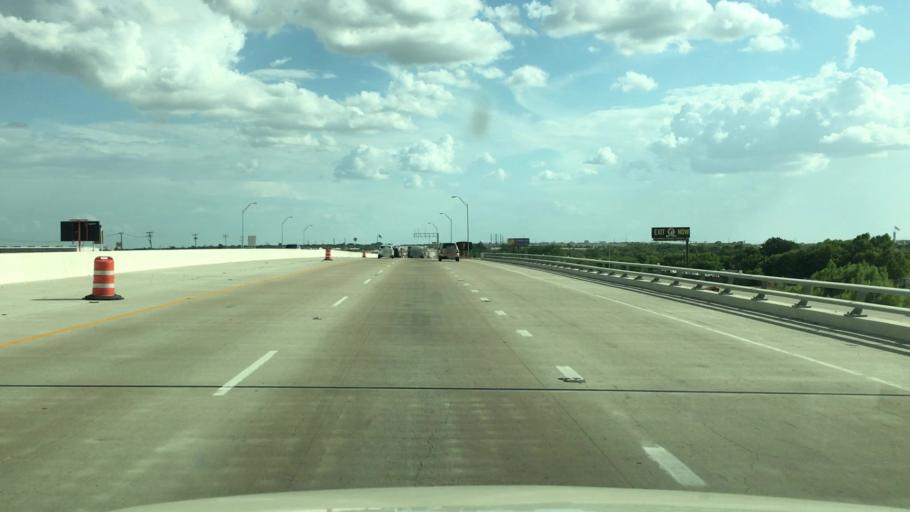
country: US
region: Texas
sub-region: Bell County
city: Troy
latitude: 31.1556
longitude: -97.3240
